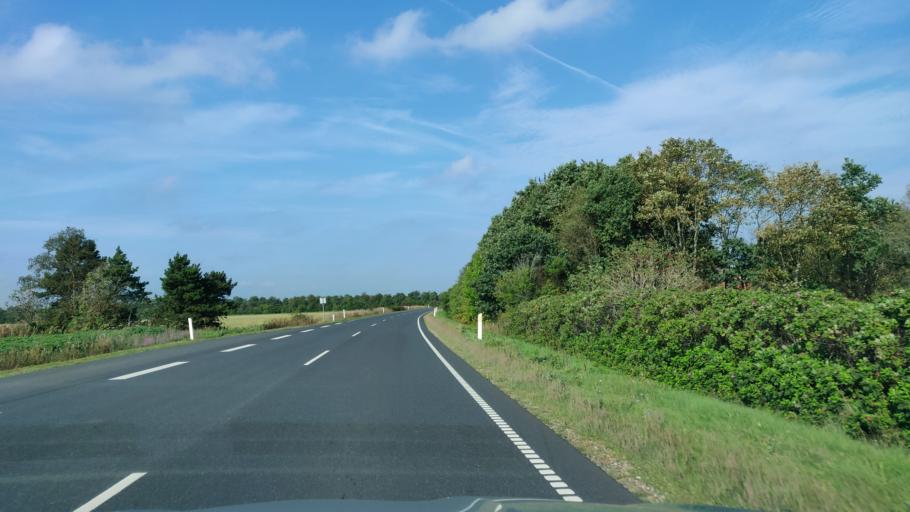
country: DK
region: Central Jutland
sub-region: Herning Kommune
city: Sunds
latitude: 56.2666
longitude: 8.9910
